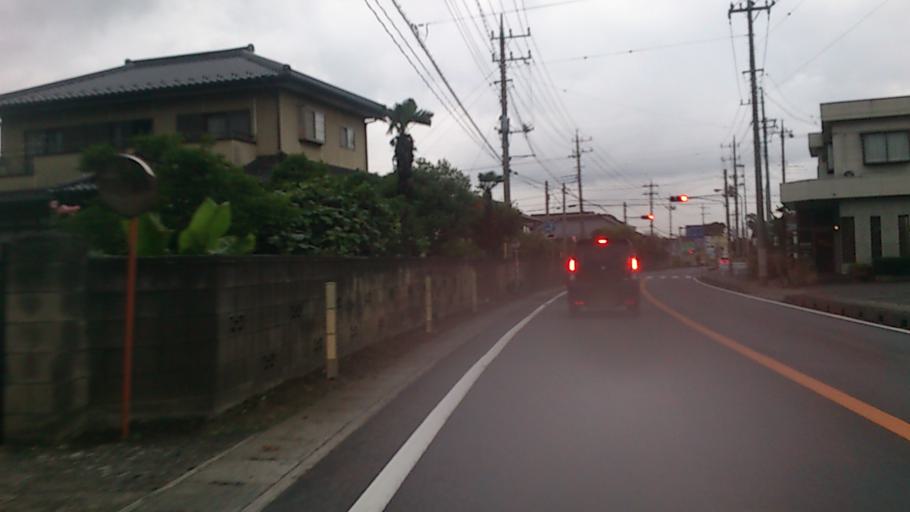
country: JP
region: Ibaraki
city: Koga
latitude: 36.1573
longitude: 139.7481
